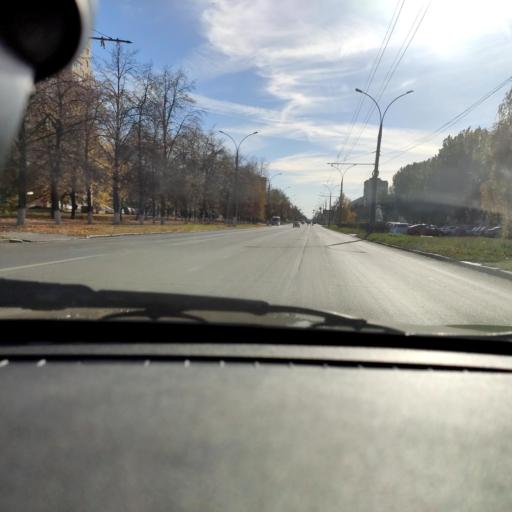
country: RU
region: Samara
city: Tol'yatti
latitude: 53.5328
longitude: 49.2770
